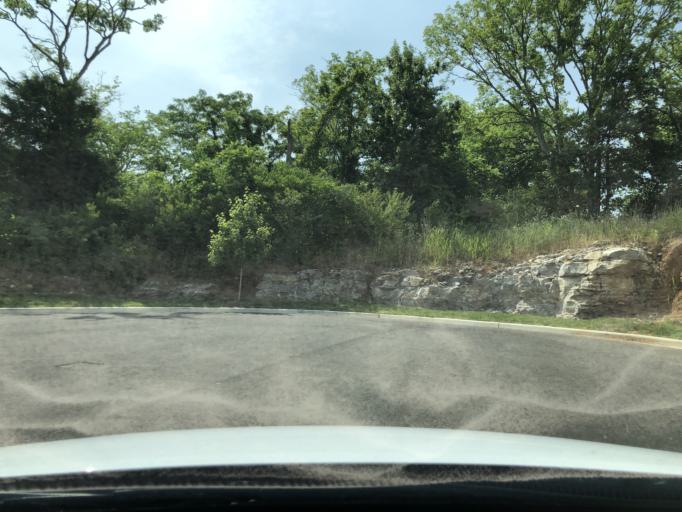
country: US
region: Tennessee
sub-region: Rutherford County
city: La Vergne
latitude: 36.0606
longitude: -86.6706
